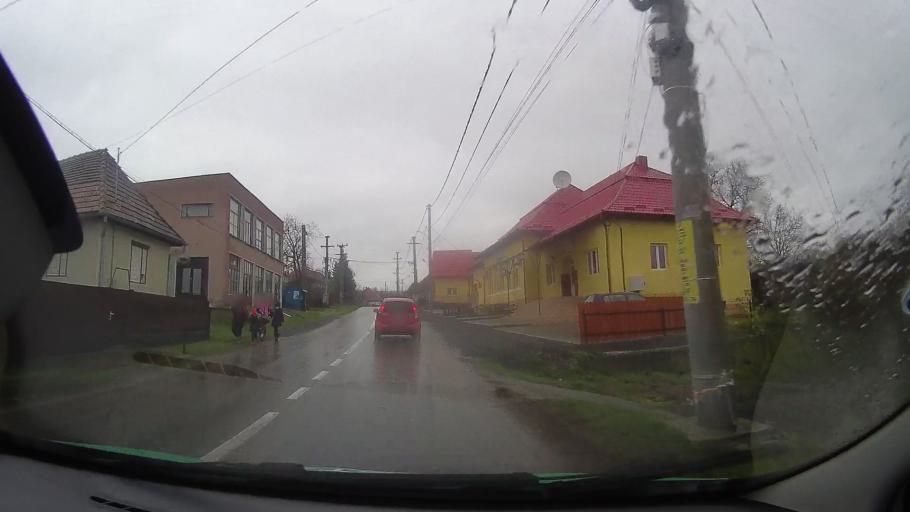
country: RO
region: Mures
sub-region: Comuna Vatava
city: Vatava
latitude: 46.9425
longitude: 24.7651
